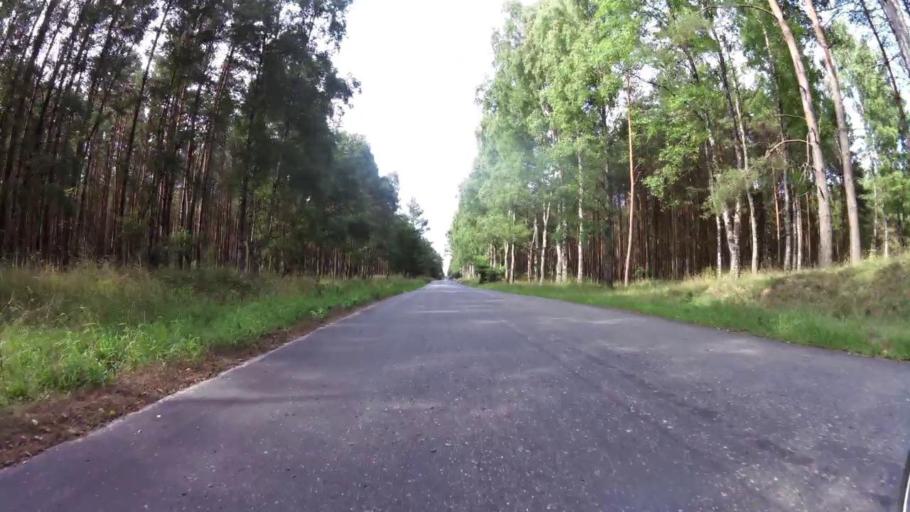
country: PL
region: West Pomeranian Voivodeship
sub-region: Powiat stargardzki
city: Insko
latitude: 53.3848
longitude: 15.5964
